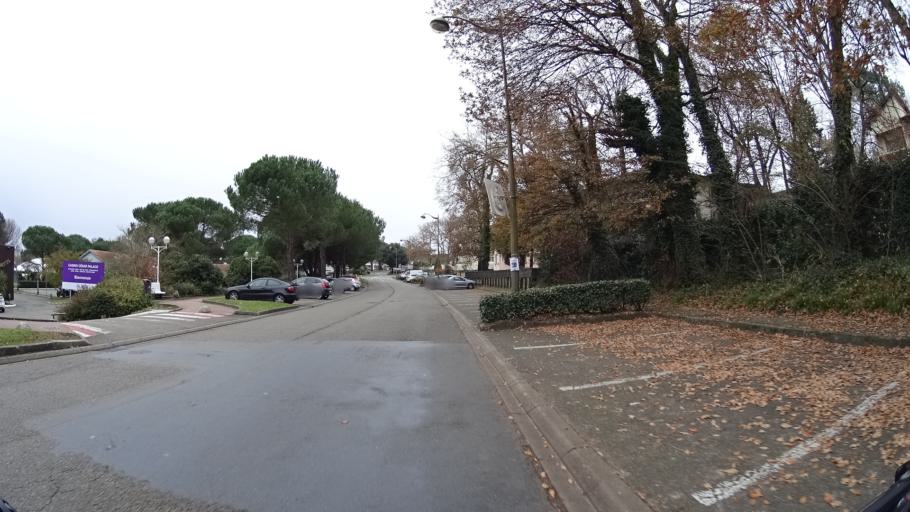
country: FR
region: Aquitaine
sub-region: Departement des Landes
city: Saint-Paul-les-Dax
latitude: 43.7263
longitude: -1.0635
